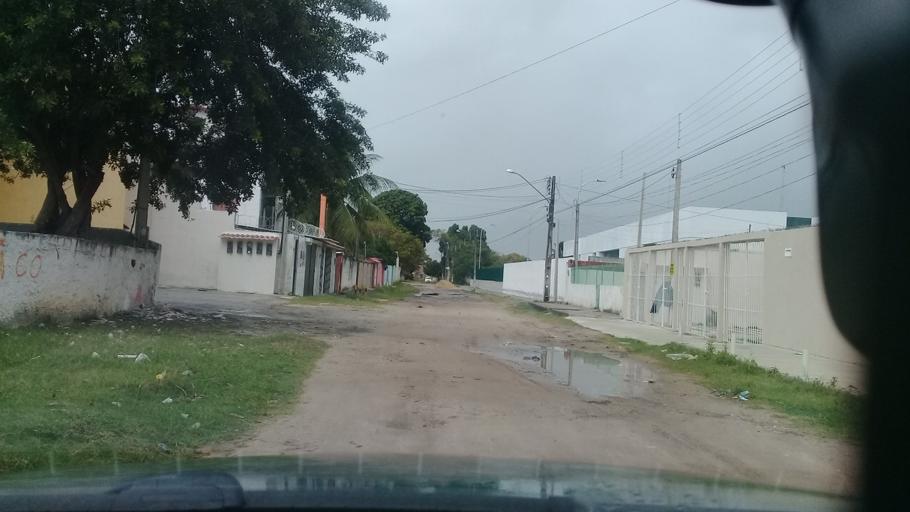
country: BR
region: Pernambuco
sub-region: Itamaraca
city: Itamaraca
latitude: -7.7365
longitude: -34.8279
